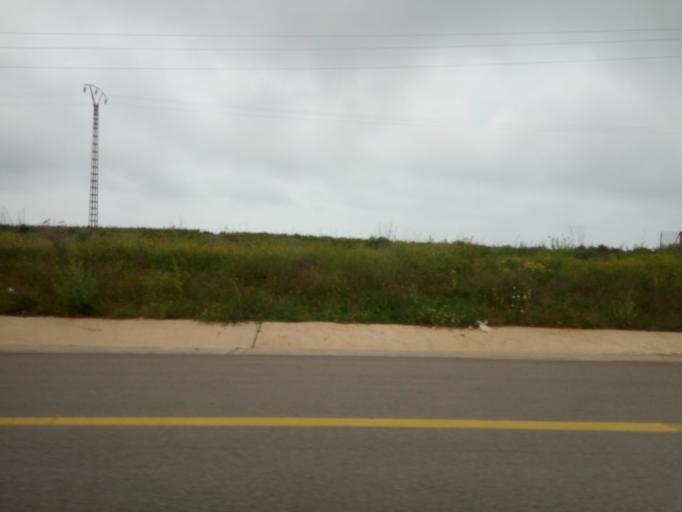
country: DZ
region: Tipaza
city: Bou Ismail
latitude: 36.5960
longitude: 2.6346
